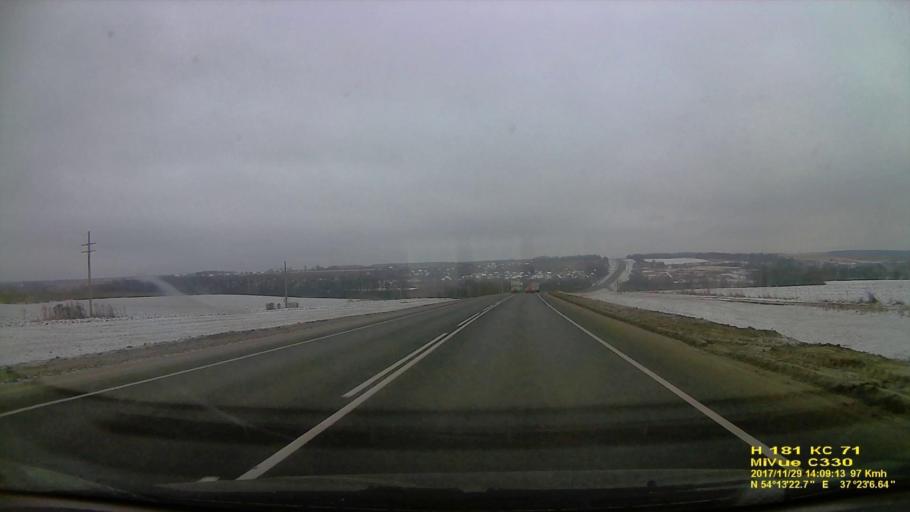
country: RU
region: Tula
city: Leninskiy
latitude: 54.2229
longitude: 37.3854
